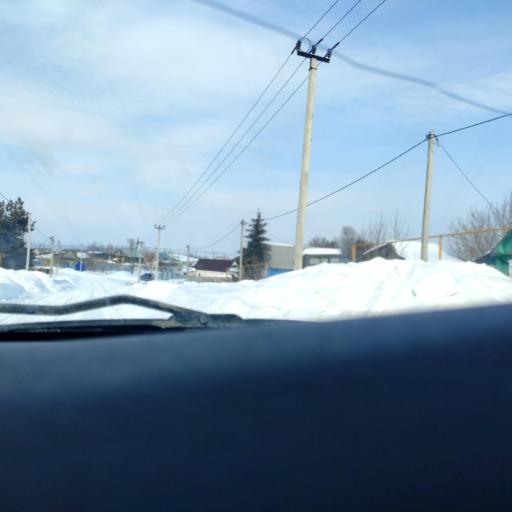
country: RU
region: Samara
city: Rozhdestveno
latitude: 53.2444
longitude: 50.0629
